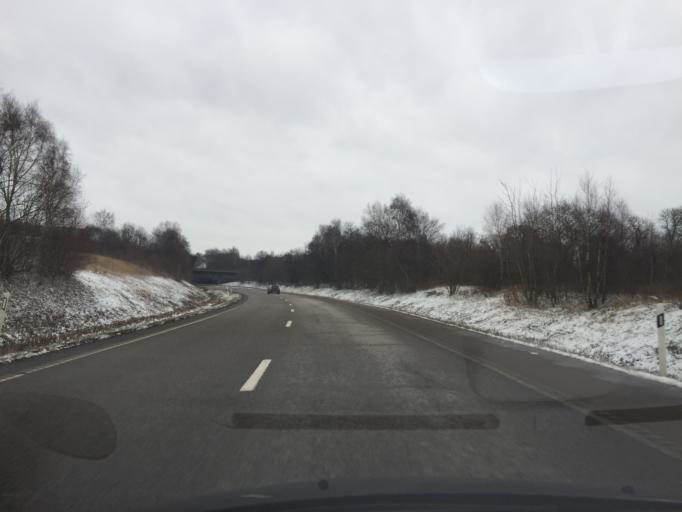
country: SE
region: Skane
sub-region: Helsingborg
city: Odakra
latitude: 56.0861
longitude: 12.7757
